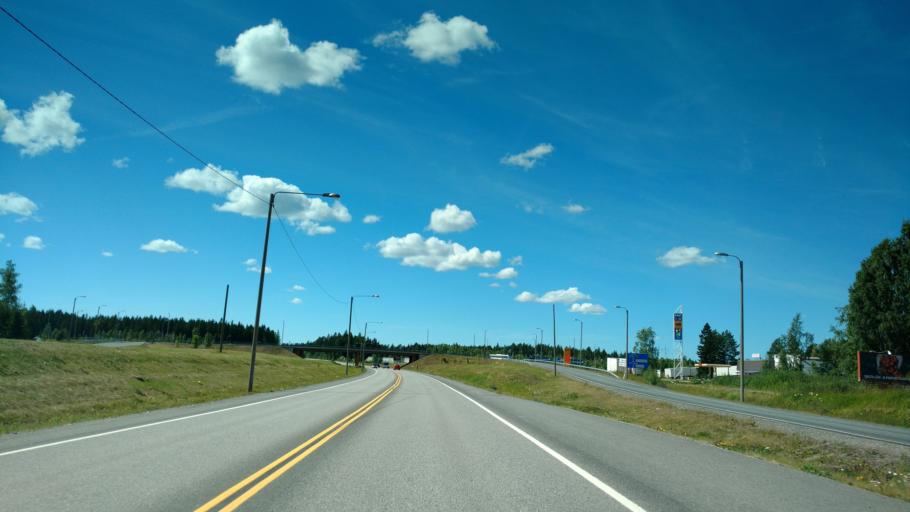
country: FI
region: Varsinais-Suomi
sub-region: Turku
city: Lieto
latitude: 60.4639
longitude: 22.4166
